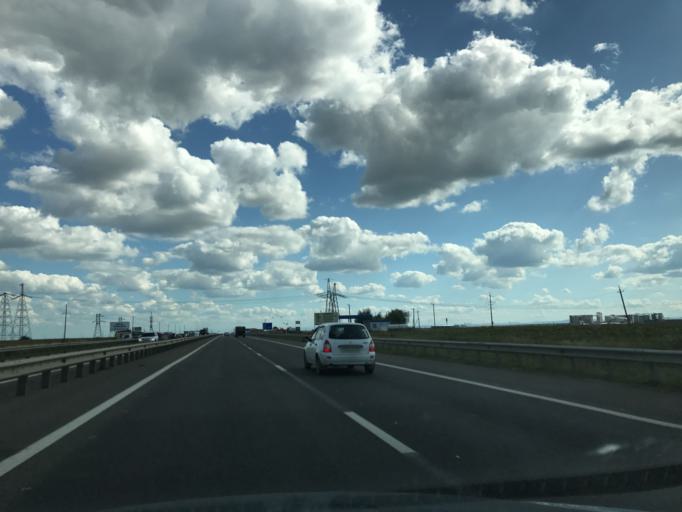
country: RU
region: Adygeya
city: Adygeysk
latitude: 44.8544
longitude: 39.2006
